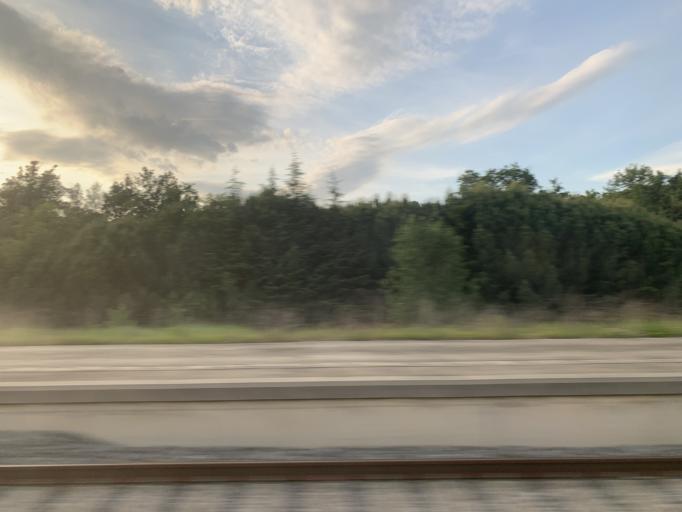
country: ES
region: Catalonia
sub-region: Provincia de Girona
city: Breda
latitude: 41.7289
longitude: 2.5771
